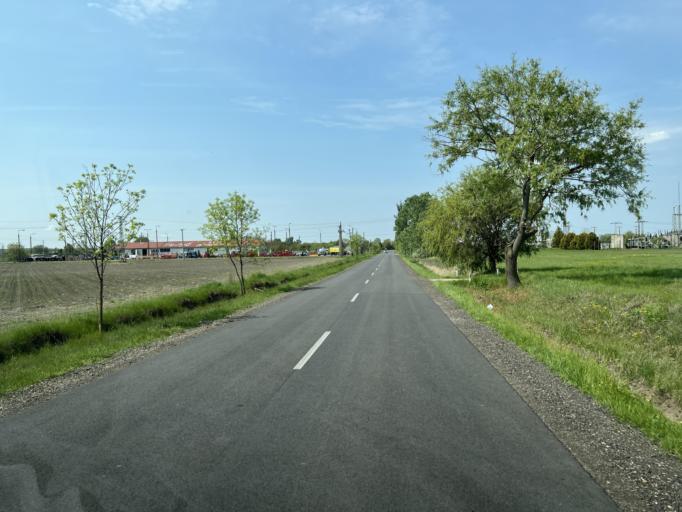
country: HU
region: Pest
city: Nagykoros
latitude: 47.0316
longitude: 19.8158
